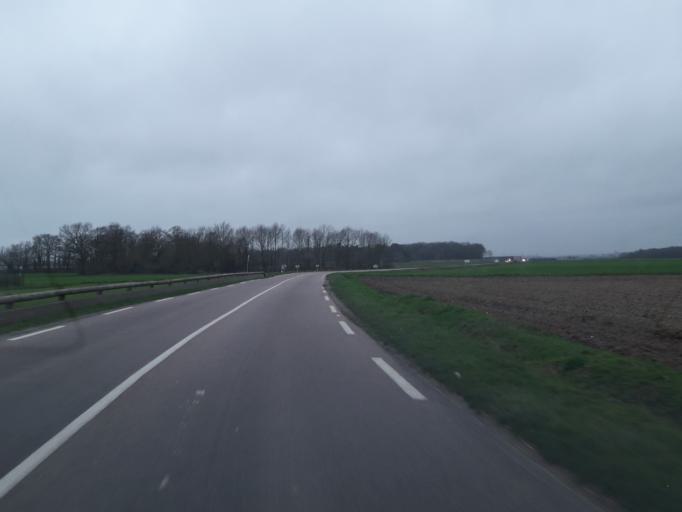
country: FR
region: Ile-de-France
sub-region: Departement de l'Essonne
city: Leudeville
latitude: 48.5719
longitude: 2.3257
